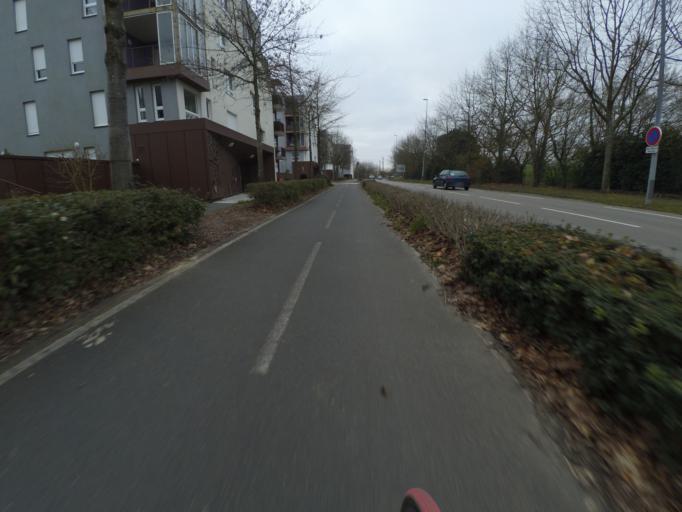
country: FR
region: Pays de la Loire
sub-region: Departement de la Loire-Atlantique
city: Carquefou
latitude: 47.2900
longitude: -1.4851
